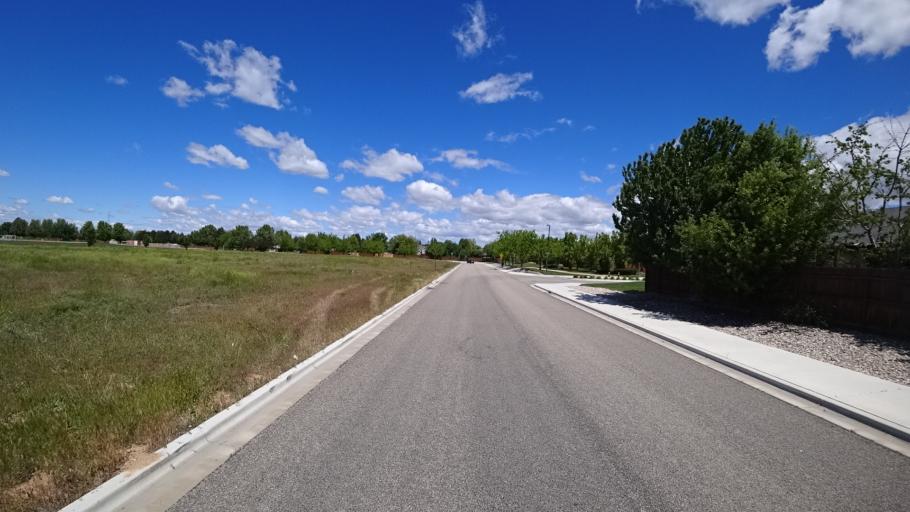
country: US
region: Idaho
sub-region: Ada County
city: Meridian
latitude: 43.6394
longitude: -116.3496
